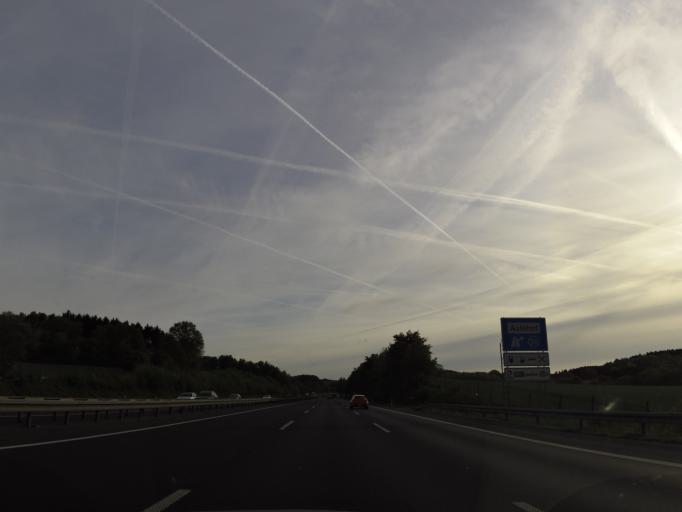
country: DE
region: Hesse
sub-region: Regierungsbezirk Kassel
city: Fuldatal
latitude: 51.3561
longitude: 9.6120
